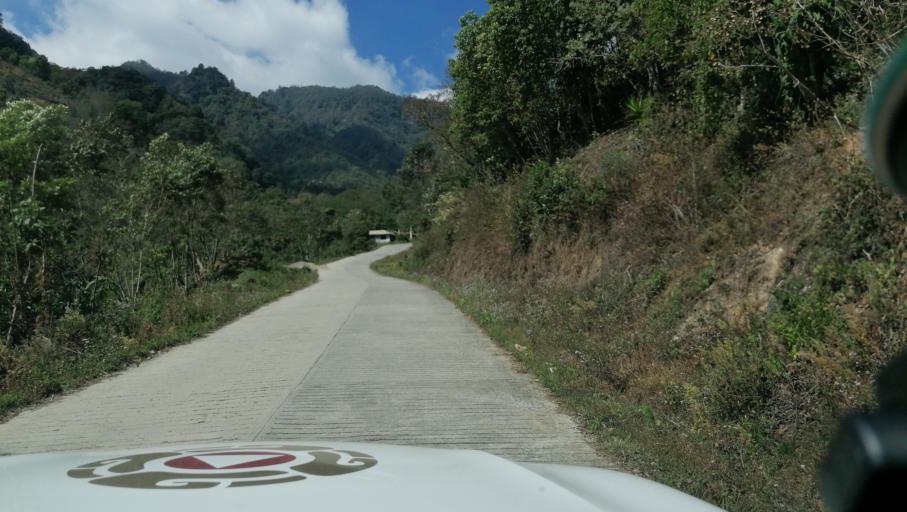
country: GT
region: San Marcos
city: Tacana
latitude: 15.2024
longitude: -92.1990
